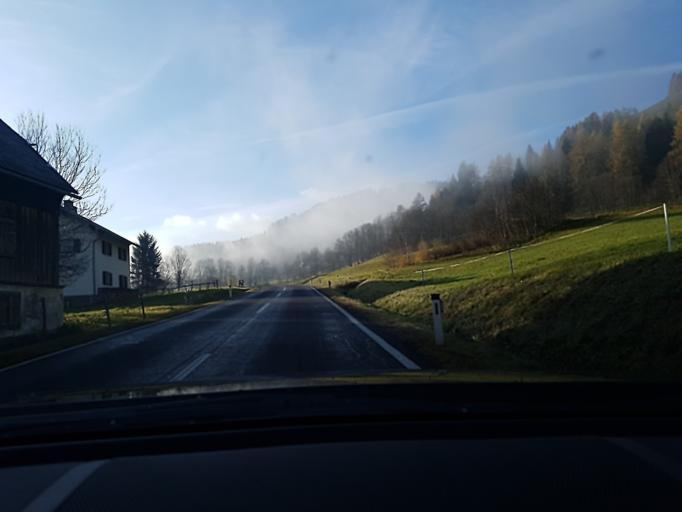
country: AT
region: Styria
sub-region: Politischer Bezirk Murau
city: Schoder
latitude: 47.1734
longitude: 14.1137
